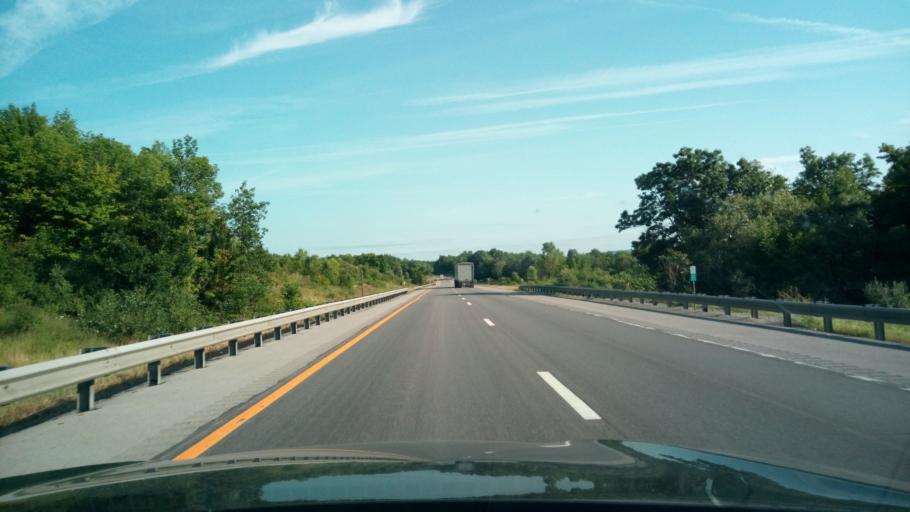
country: US
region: New York
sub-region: Livingston County
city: Dansville
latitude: 42.5916
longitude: -77.7483
